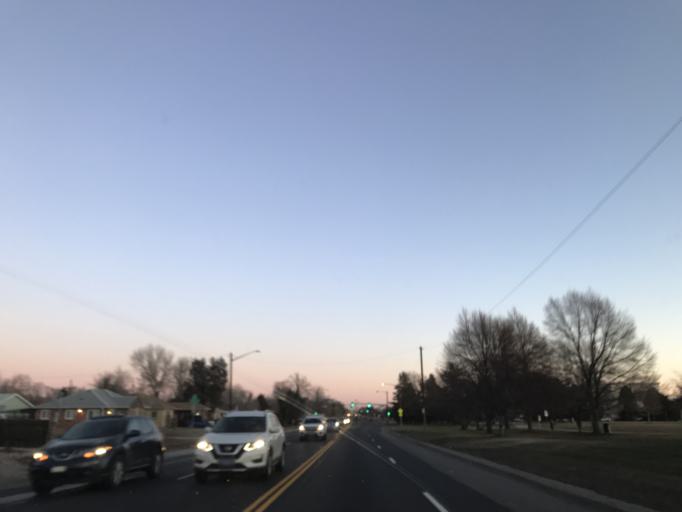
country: US
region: Colorado
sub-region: Arapahoe County
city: Glendale
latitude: 39.7529
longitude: -104.9034
